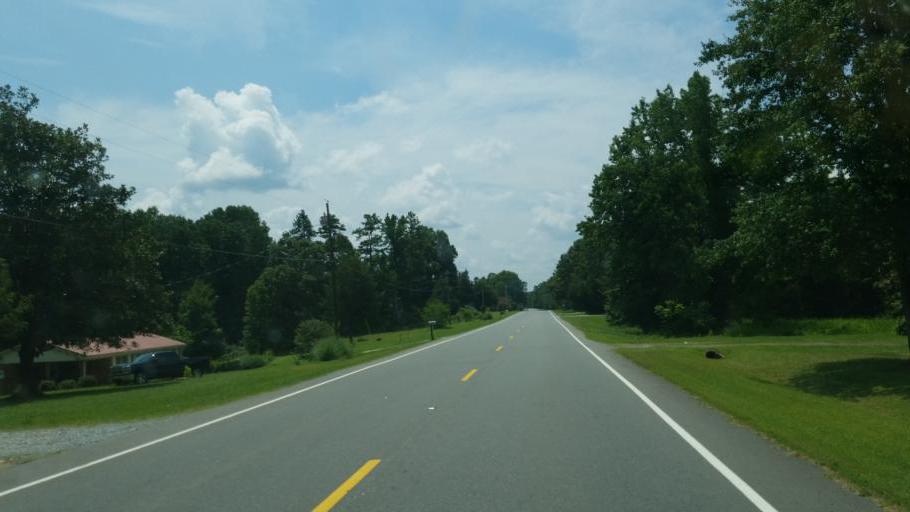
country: US
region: North Carolina
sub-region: Cleveland County
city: Kings Mountain
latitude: 35.1713
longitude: -81.3269
